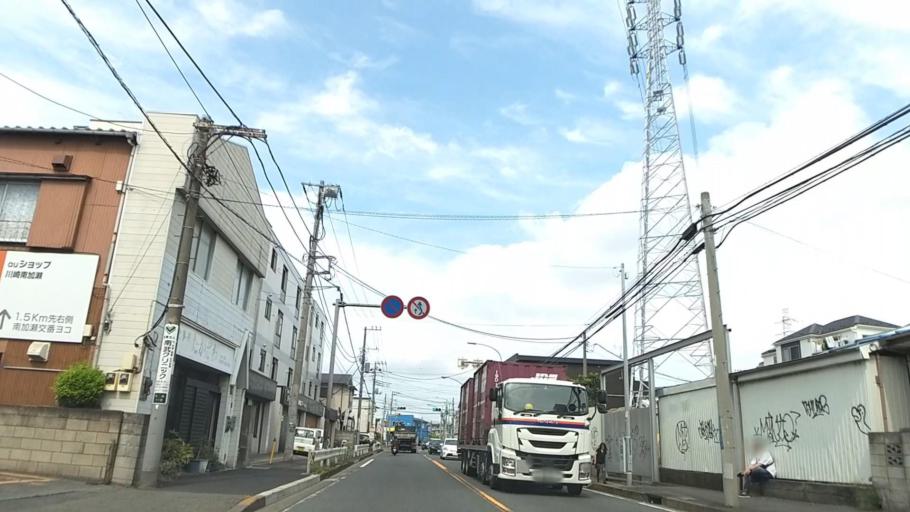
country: JP
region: Kanagawa
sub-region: Kawasaki-shi
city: Kawasaki
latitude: 35.5296
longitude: 139.6750
